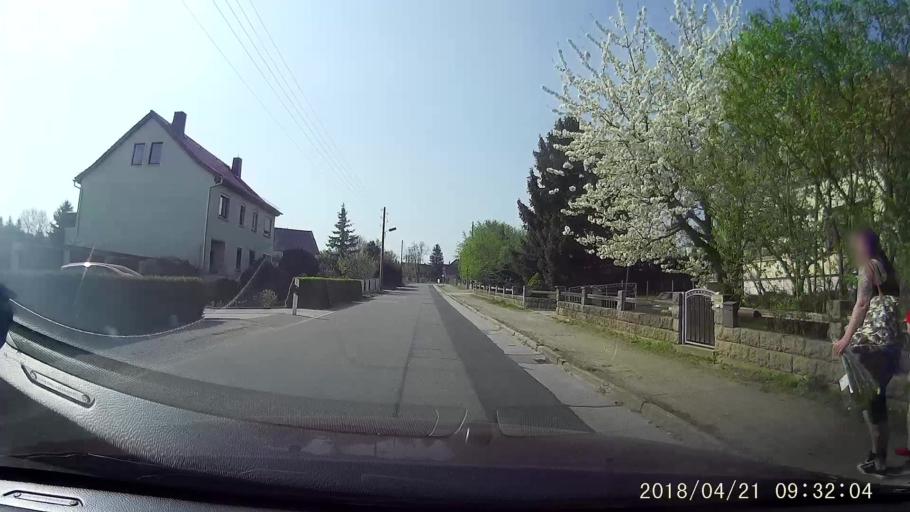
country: DE
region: Saxony
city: Radibor
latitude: 51.2091
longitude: 14.3938
